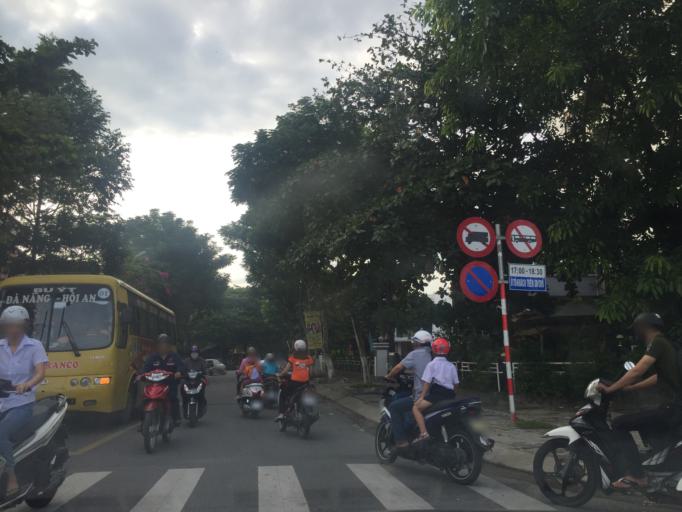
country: VN
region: Da Nang
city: Da Nang
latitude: 16.0803
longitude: 108.2111
